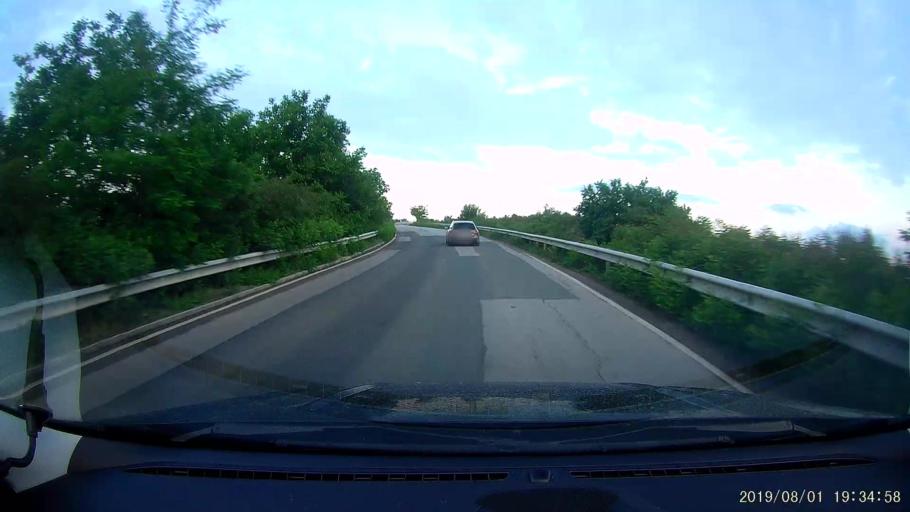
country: BG
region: Burgas
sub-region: Obshtina Sungurlare
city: Sungurlare
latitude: 42.7662
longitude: 26.8795
